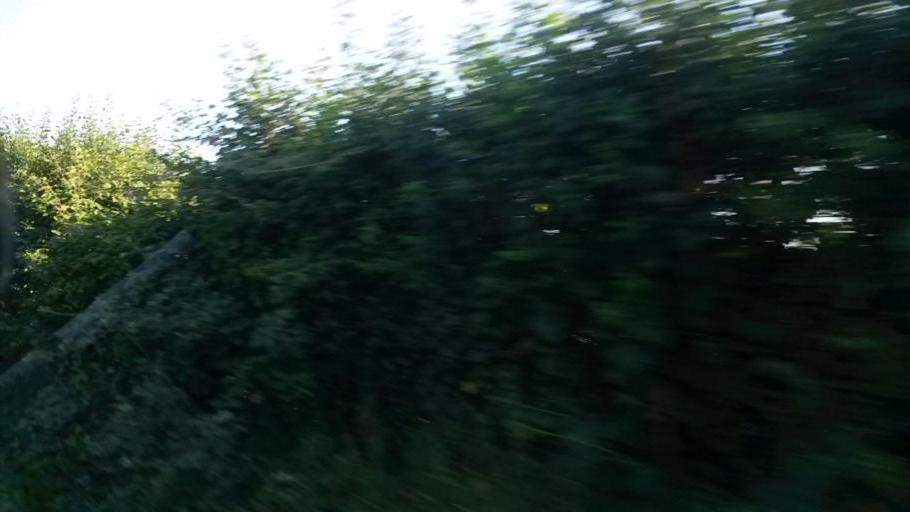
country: IE
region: Leinster
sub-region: An Mhi
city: Ashbourne
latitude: 53.5387
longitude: -6.3682
